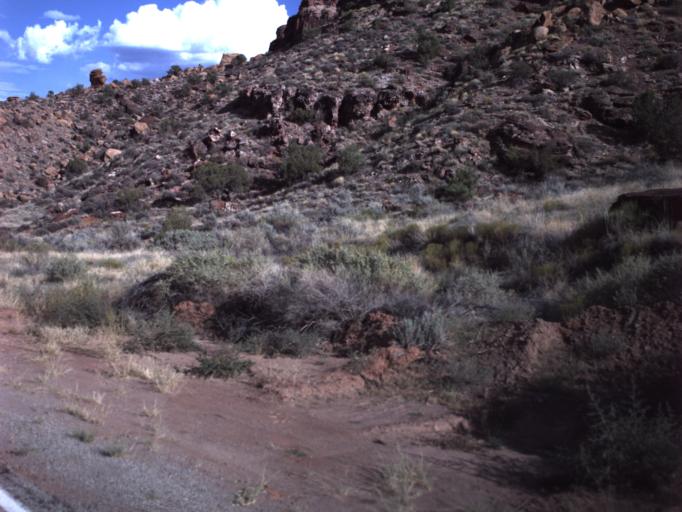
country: US
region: Utah
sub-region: Grand County
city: Moab
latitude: 38.6846
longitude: -109.4653
